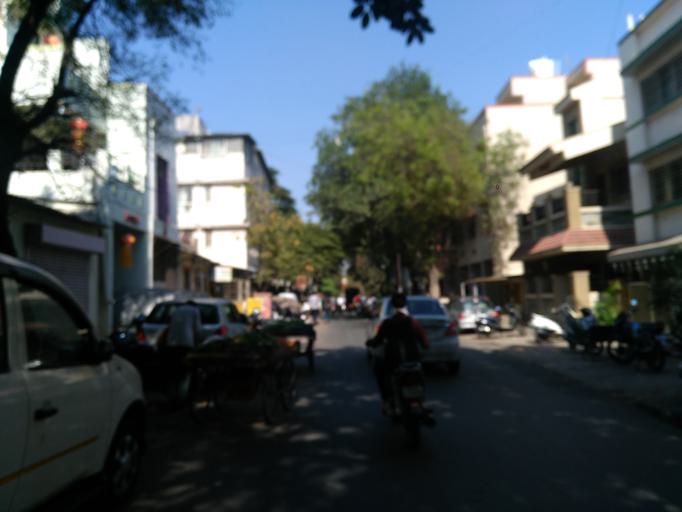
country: IN
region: Maharashtra
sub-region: Pune Division
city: Pune
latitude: 18.4934
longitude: 73.8487
